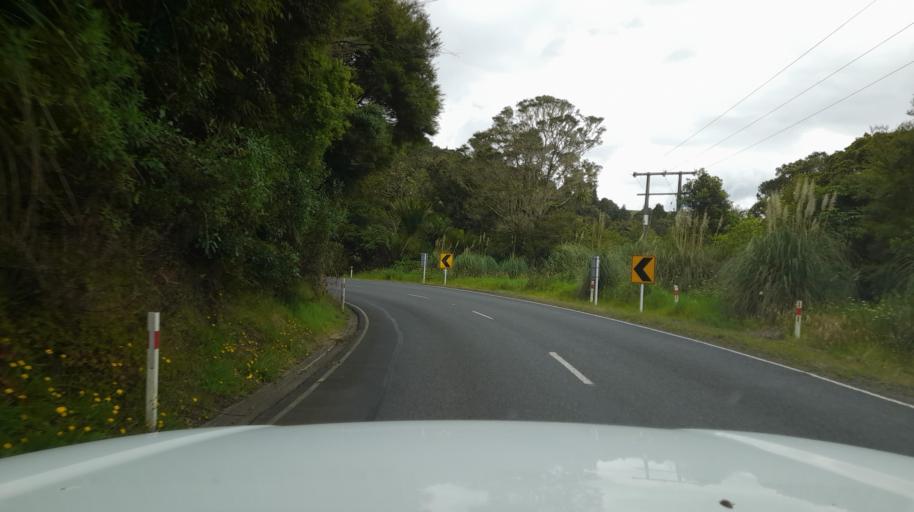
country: NZ
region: Northland
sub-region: Far North District
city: Taipa
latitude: -35.2551
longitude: 173.5346
